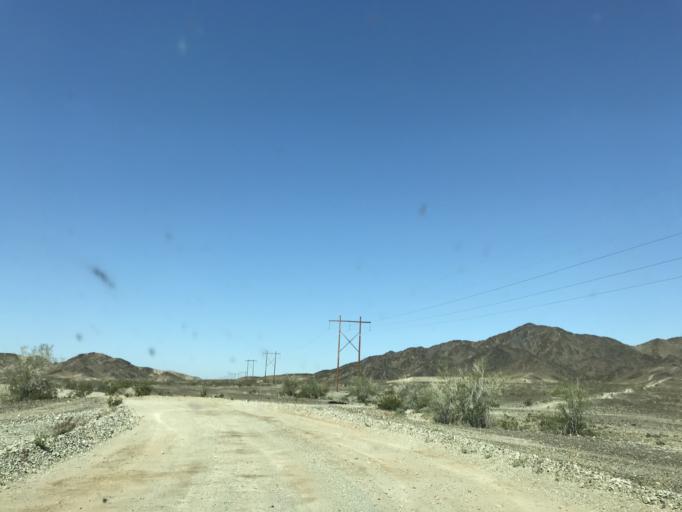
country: US
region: California
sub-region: Riverside County
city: Mesa Verde
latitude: 33.4946
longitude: -114.8212
